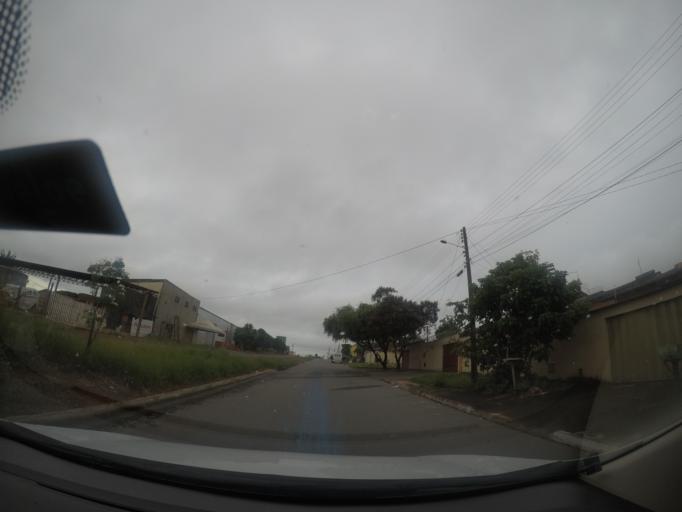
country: BR
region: Goias
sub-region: Goiania
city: Goiania
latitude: -16.7531
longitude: -49.3197
